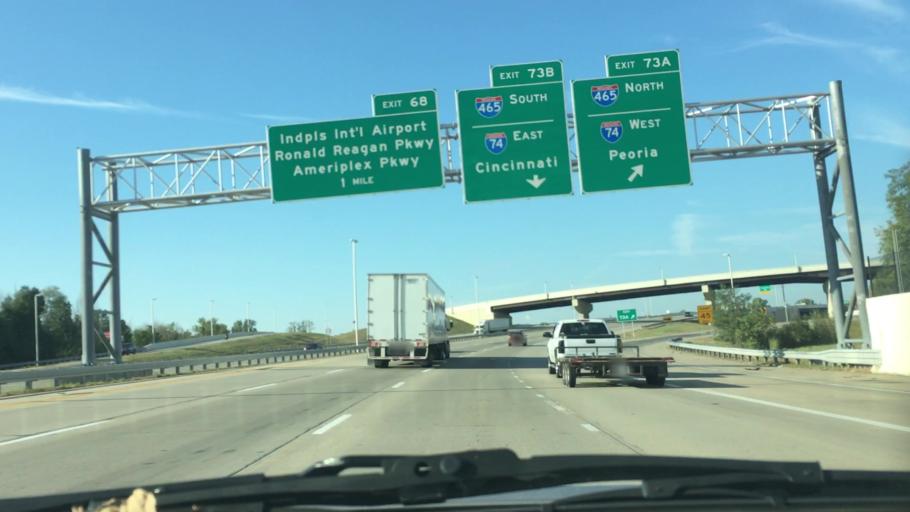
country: US
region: Indiana
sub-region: Marion County
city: Speedway
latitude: 39.7155
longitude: -86.2602
